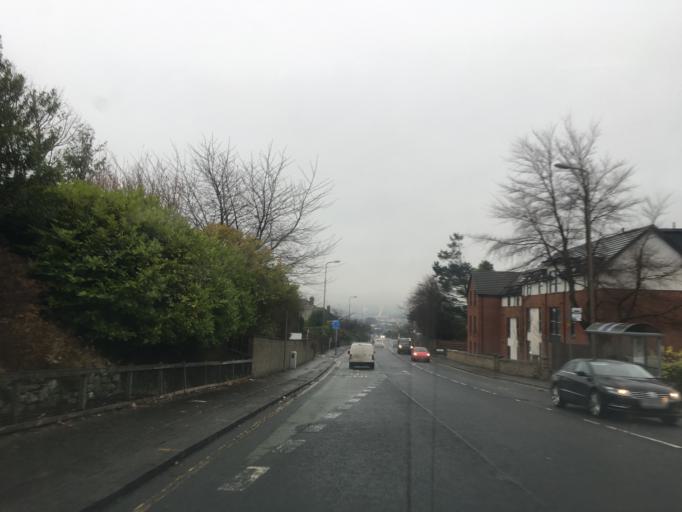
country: GB
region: Scotland
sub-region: Edinburgh
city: Currie
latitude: 55.9475
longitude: -3.2945
